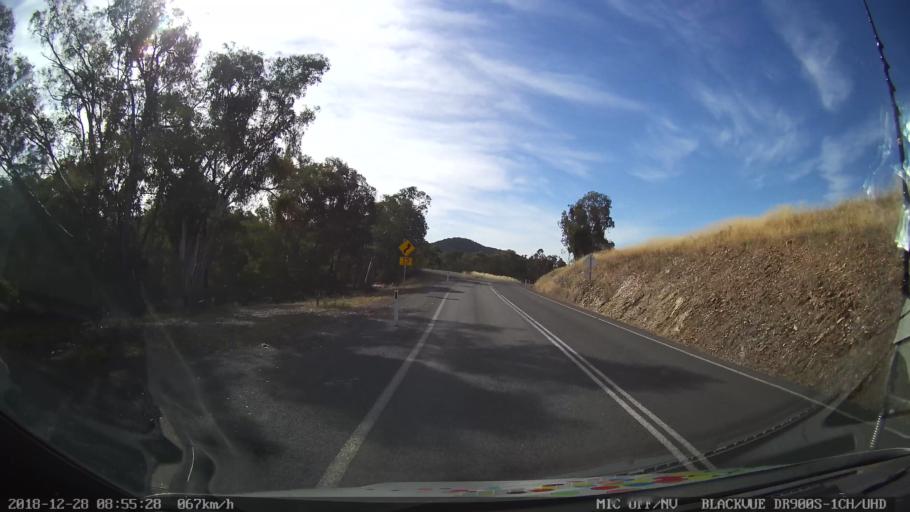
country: AU
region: New South Wales
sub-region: Upper Lachlan Shire
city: Crookwell
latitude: -34.1010
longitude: 149.3328
